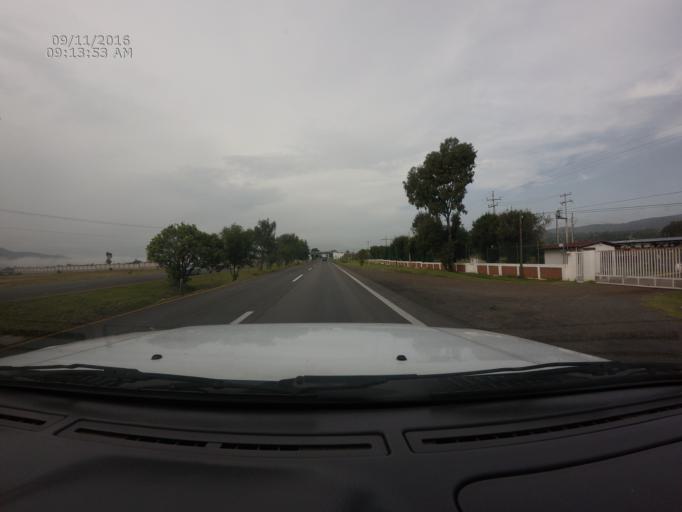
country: MX
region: Michoacan
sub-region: Morelia
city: La Mintzita (Piedra Dura)
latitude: 19.5781
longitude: -101.3124
